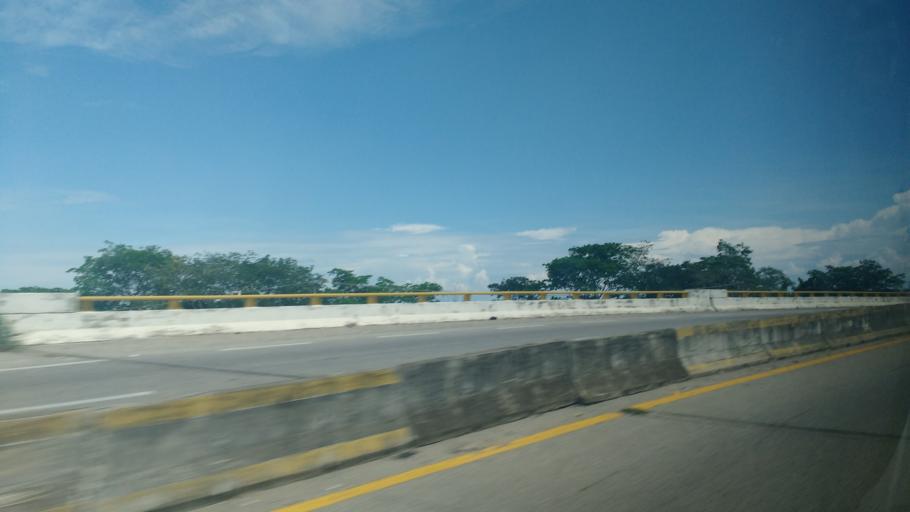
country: MX
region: Tabasco
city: Parrilla
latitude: 17.9081
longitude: -92.9225
